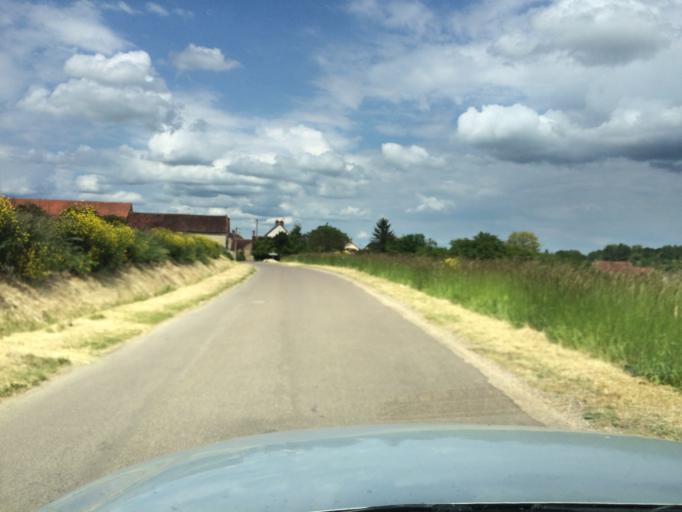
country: FR
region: Bourgogne
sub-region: Departement de l'Yonne
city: Fleury-la-Vallee
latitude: 47.8894
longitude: 3.4236
